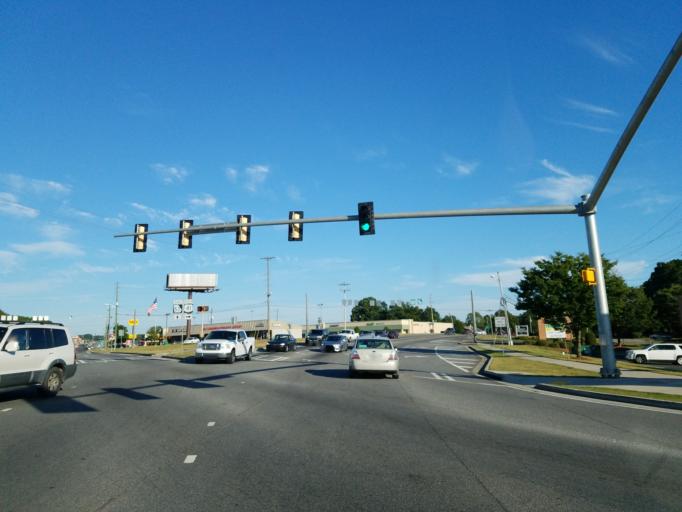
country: US
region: Georgia
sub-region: Gordon County
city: Calhoun
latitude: 34.4788
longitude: -84.9353
